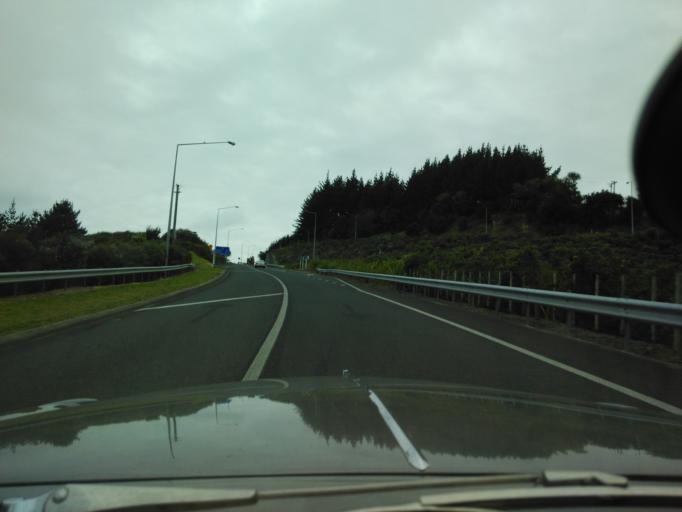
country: NZ
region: Auckland
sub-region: Auckland
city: Warkworth
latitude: -36.5328
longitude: 174.6798
